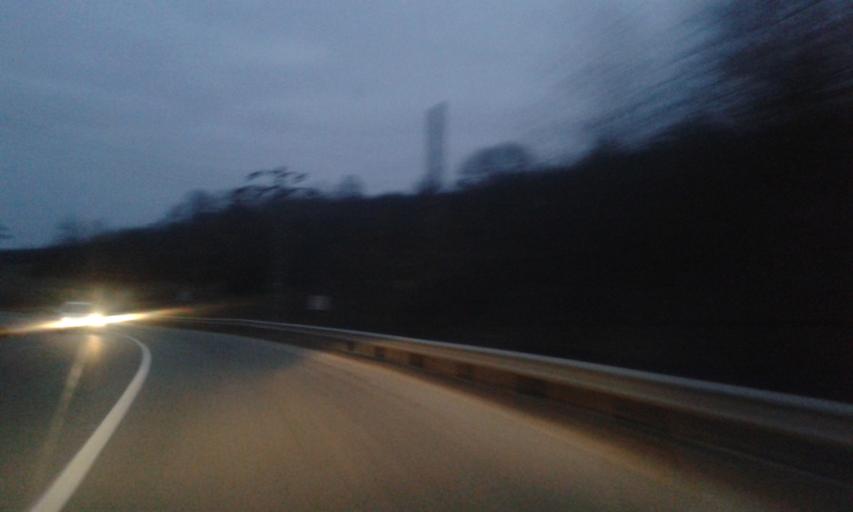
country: RO
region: Gorj
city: Targu Jiu
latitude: 45.0581
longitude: 23.2670
